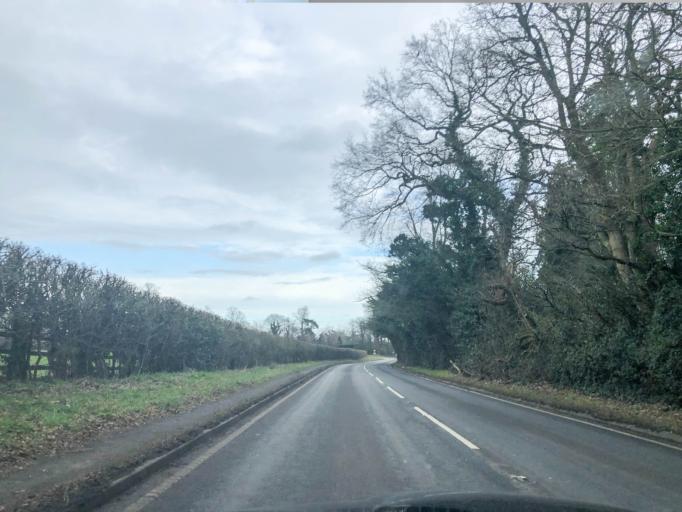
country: GB
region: England
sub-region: Warwickshire
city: Wroxall
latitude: 52.3020
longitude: -1.6554
